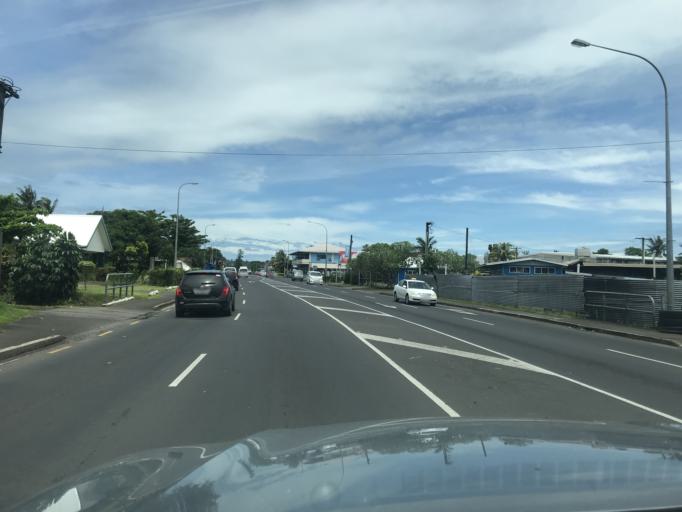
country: WS
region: Tuamasaga
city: Apia
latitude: -13.8384
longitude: -171.7716
